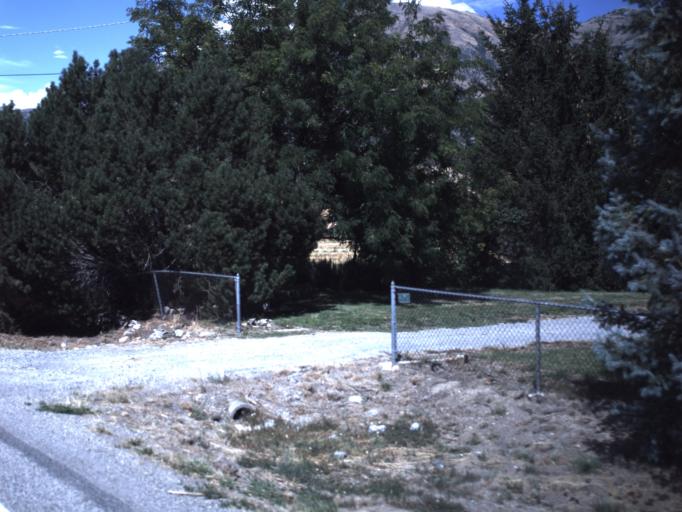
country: US
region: Utah
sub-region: Box Elder County
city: Honeyville
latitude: 41.6521
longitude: -112.0849
